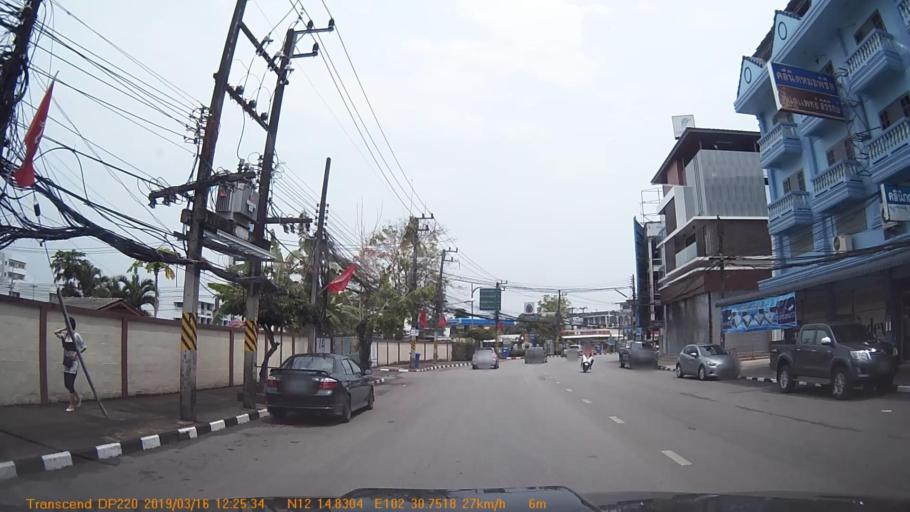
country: TH
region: Trat
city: Trat
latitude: 12.2472
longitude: 102.5126
